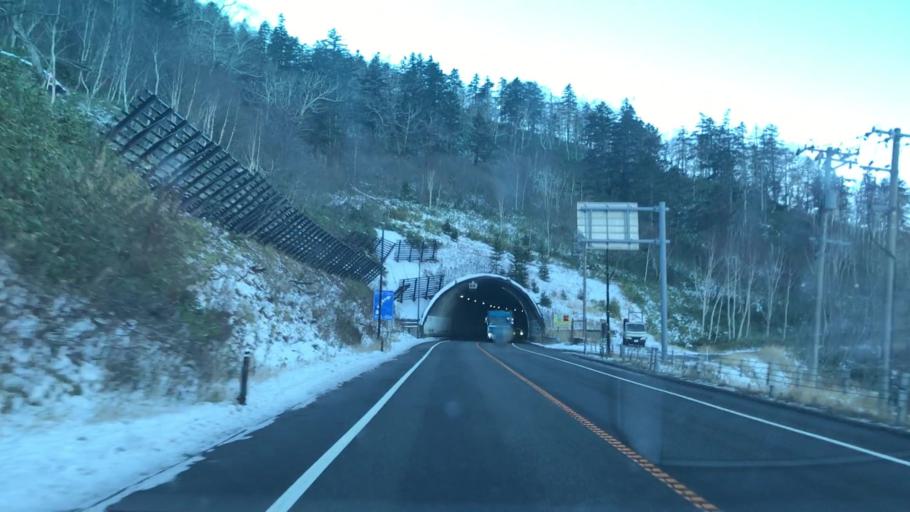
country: JP
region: Hokkaido
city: Otofuke
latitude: 42.9678
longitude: 142.7613
